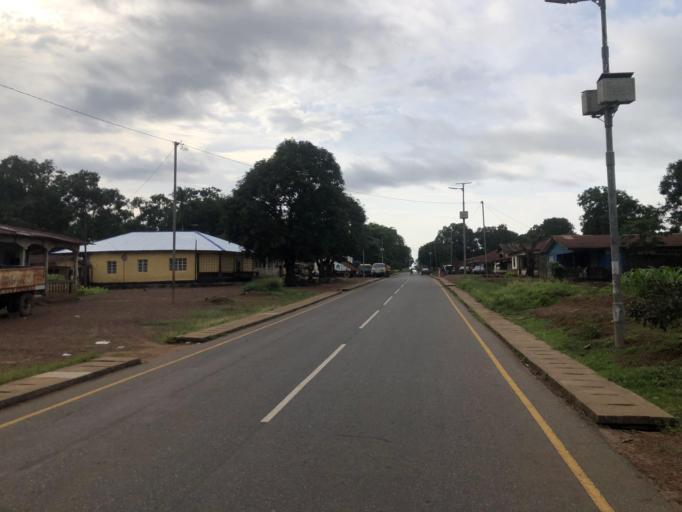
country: SL
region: Northern Province
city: Port Loko
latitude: 8.7716
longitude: -12.7915
